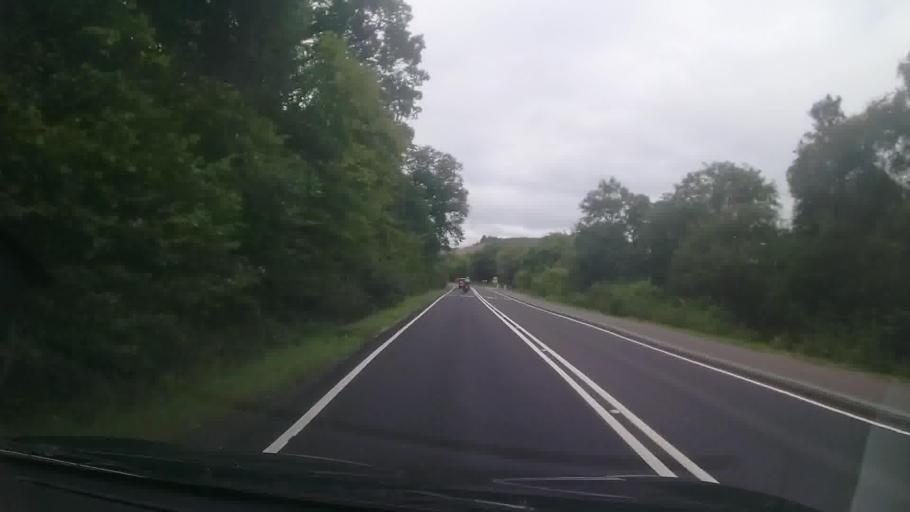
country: GB
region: Scotland
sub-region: Highland
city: Fort William
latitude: 56.7135
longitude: -5.2269
